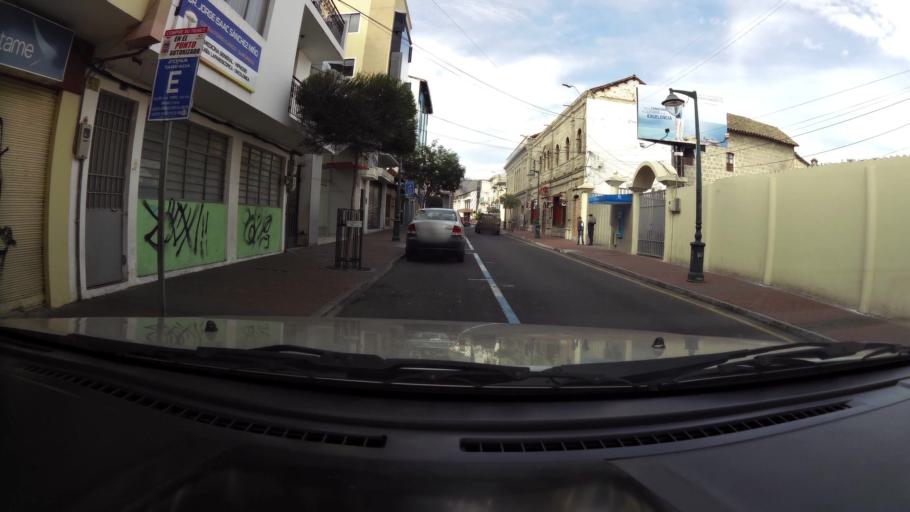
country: EC
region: Tungurahua
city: Ambato
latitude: -1.2417
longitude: -78.6272
